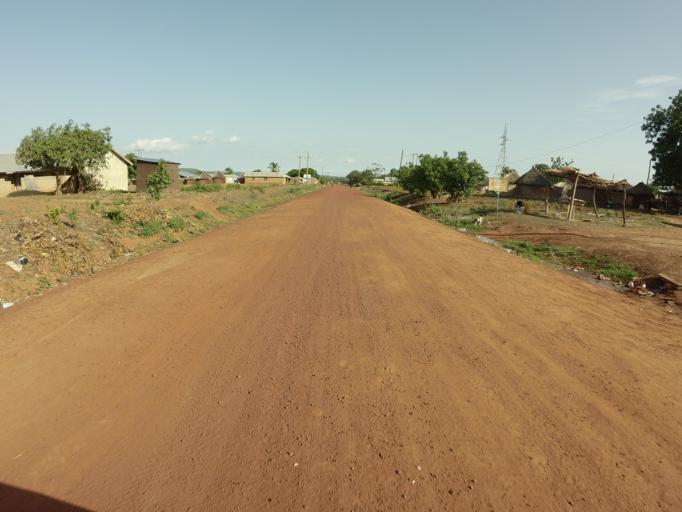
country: GH
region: Upper East
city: Bawku
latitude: 10.6280
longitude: -0.1798
